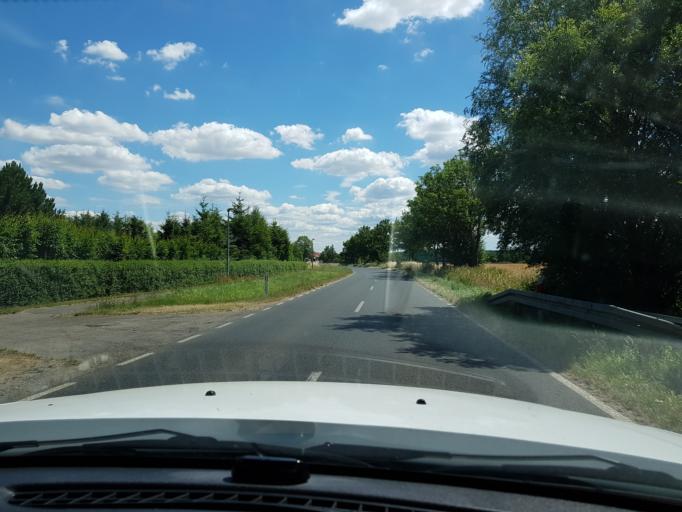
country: PL
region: West Pomeranian Voivodeship
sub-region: Powiat mysliborski
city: Mysliborz
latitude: 52.9214
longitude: 14.8983
